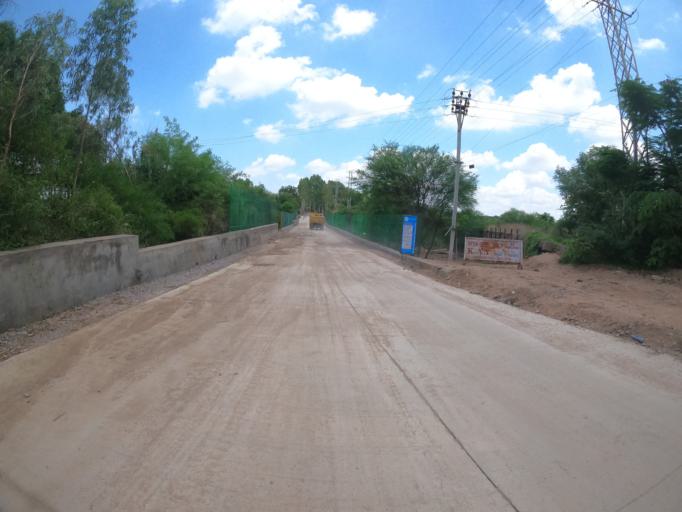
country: IN
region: Telangana
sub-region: Medak
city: Serilingampalle
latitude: 17.3794
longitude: 78.3227
